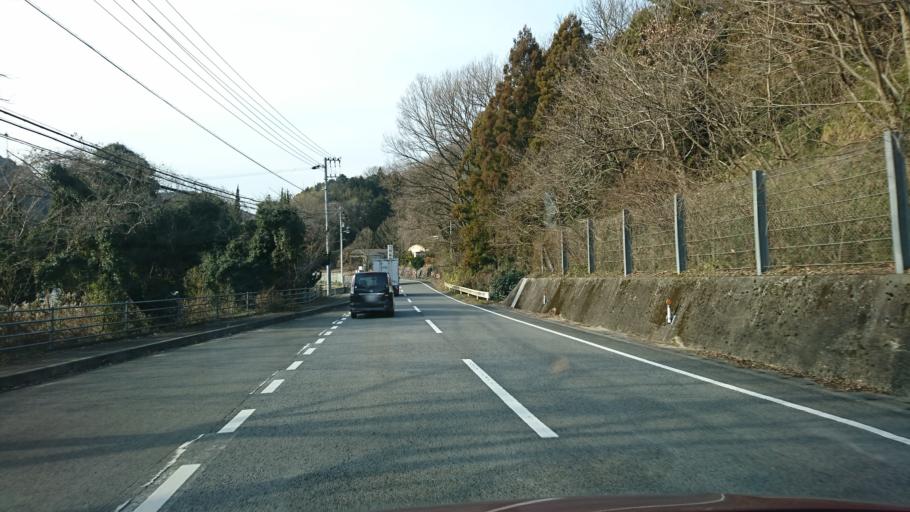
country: JP
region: Ehime
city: Hojo
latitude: 33.9959
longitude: 132.9249
